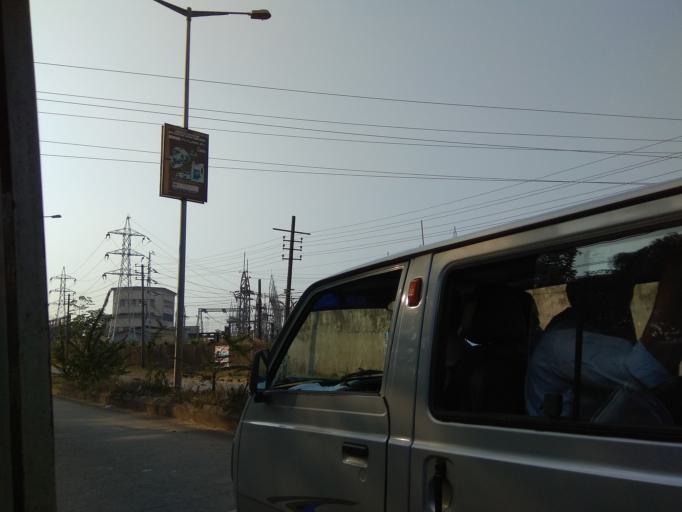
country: IN
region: Karnataka
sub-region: Dakshina Kannada
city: Mangalore
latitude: 12.9245
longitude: 74.8624
